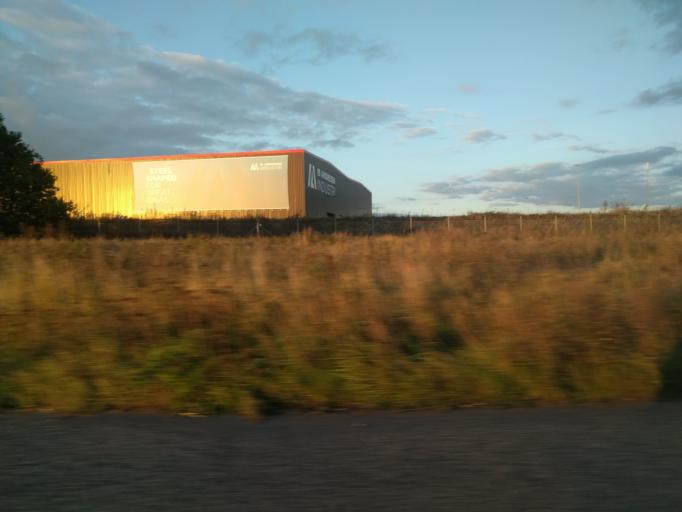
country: DK
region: South Denmark
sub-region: Kerteminde Kommune
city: Langeskov
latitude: 55.3540
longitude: 10.6156
